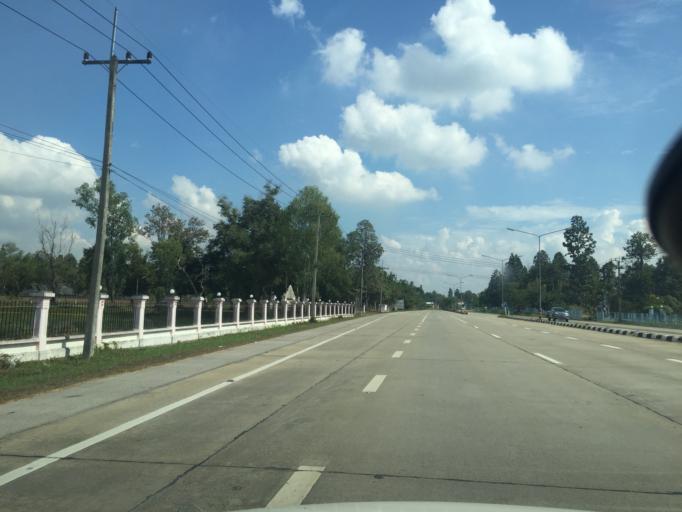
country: TH
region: Lampang
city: Hang Chat
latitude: 18.3285
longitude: 99.3757
